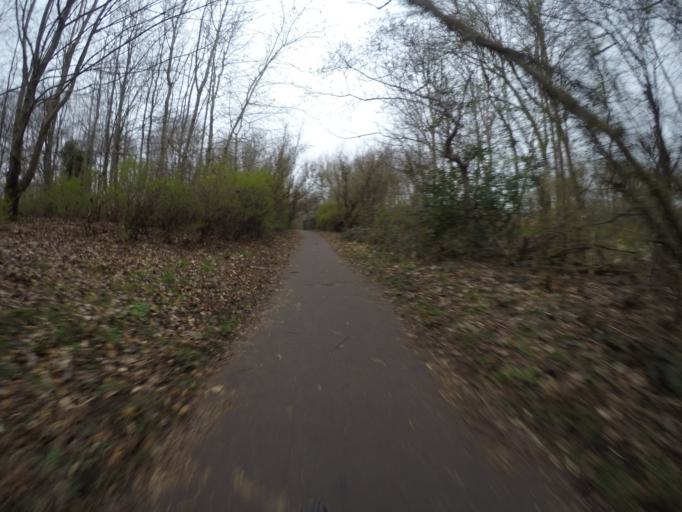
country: GB
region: Scotland
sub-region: North Ayrshire
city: Irvine
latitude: 55.6129
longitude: -4.6421
